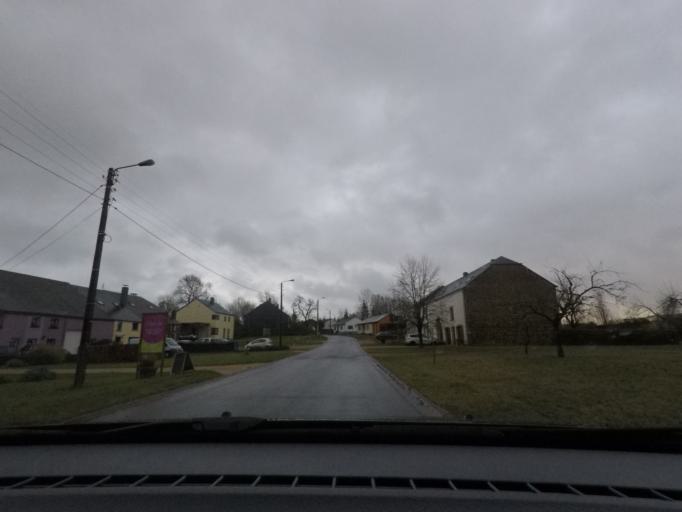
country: BE
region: Wallonia
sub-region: Province du Luxembourg
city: Tintigny
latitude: 49.7069
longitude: 5.5355
